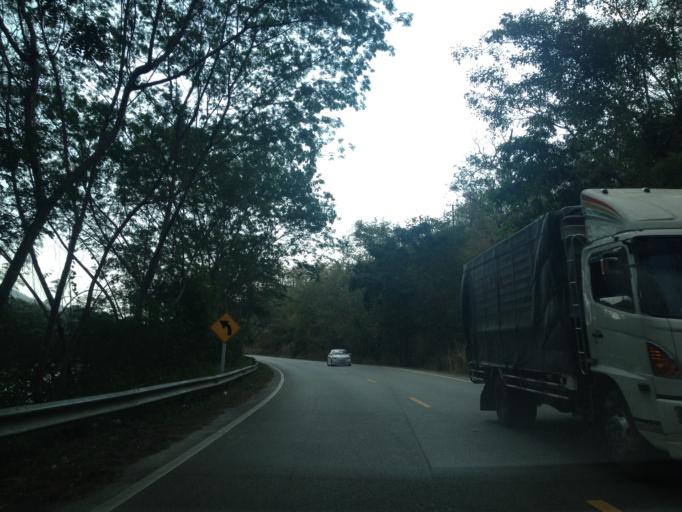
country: TH
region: Chiang Mai
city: Hot
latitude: 18.2322
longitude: 98.5559
